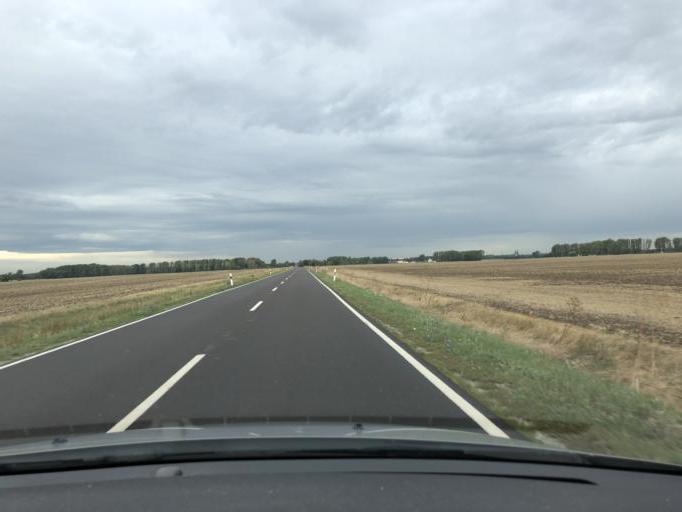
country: DE
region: Saxony-Anhalt
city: Calbe
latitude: 51.8860
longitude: 11.8216
